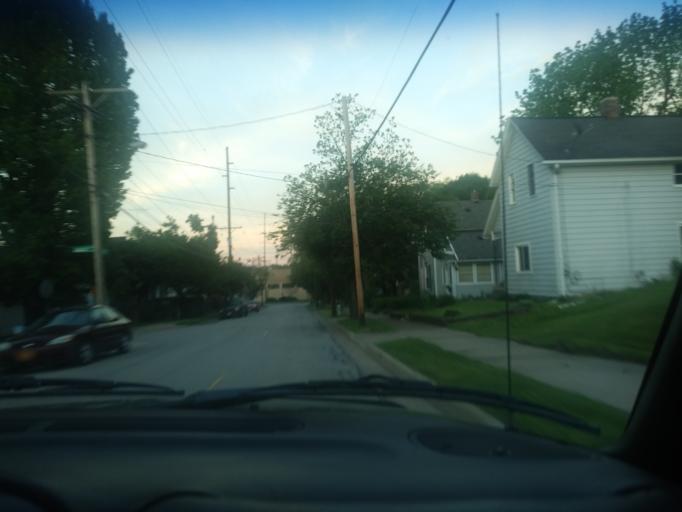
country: US
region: Ohio
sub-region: Summit County
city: Akron
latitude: 41.0801
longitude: -81.4920
